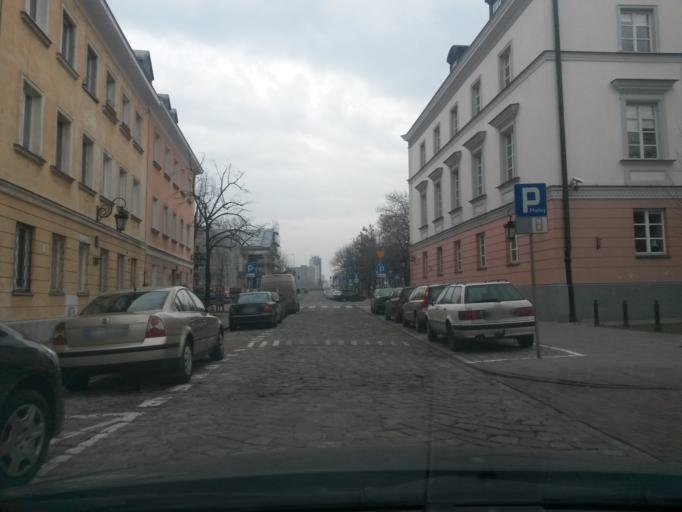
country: PL
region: Masovian Voivodeship
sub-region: Warszawa
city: Srodmiescie
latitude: 52.2455
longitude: 21.0192
